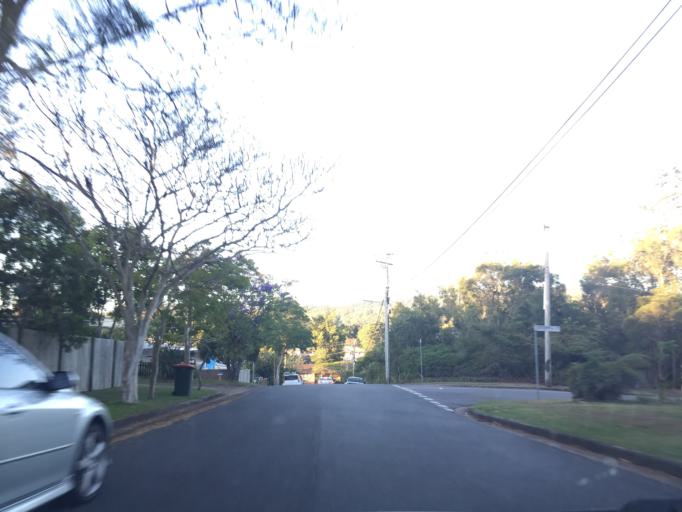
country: AU
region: Queensland
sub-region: Brisbane
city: Taringa
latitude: -27.4530
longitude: 152.9469
